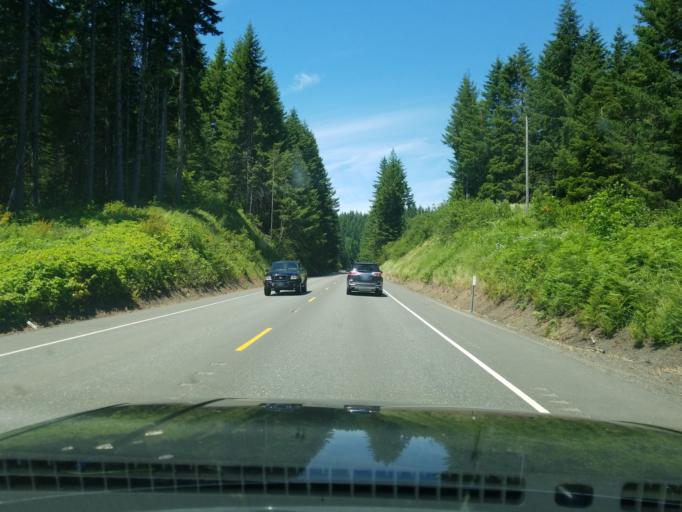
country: US
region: Oregon
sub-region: Columbia County
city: Vernonia
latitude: 45.7399
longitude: -123.2664
